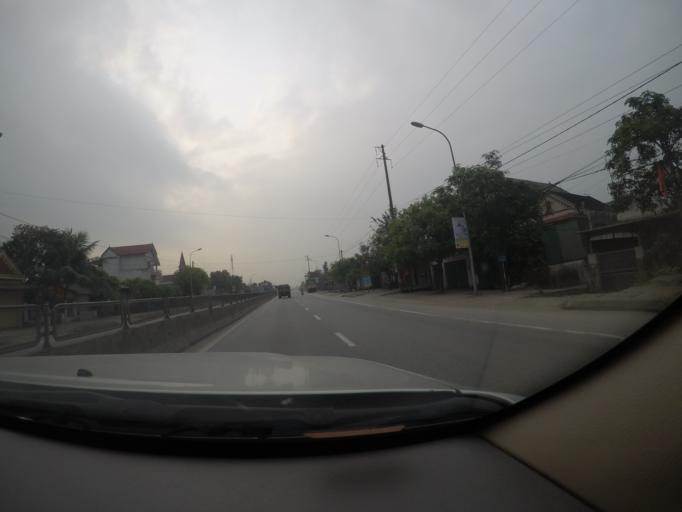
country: VN
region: Ha Tinh
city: Cam Xuyen
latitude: 18.2439
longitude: 106.0104
